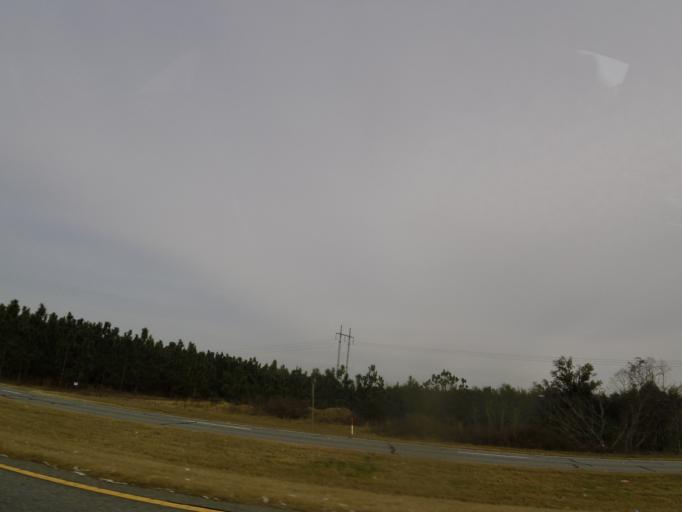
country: US
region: Georgia
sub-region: Seminole County
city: Donalsonville
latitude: 30.9840
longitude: -84.7560
